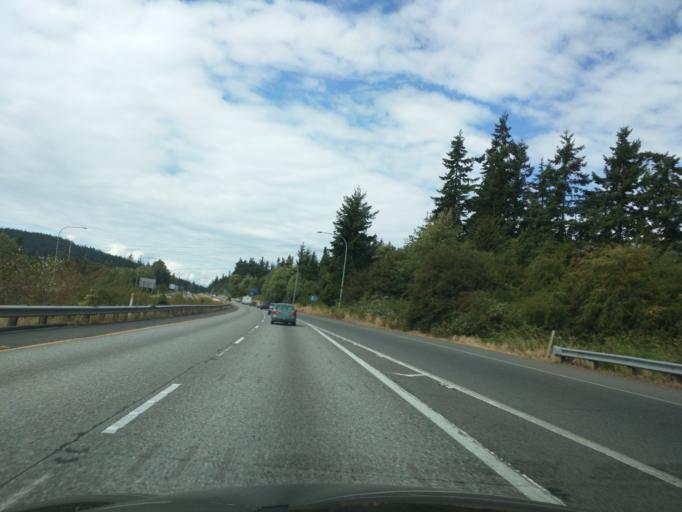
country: US
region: Washington
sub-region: Whatcom County
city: Bellingham
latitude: 48.7154
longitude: -122.4739
